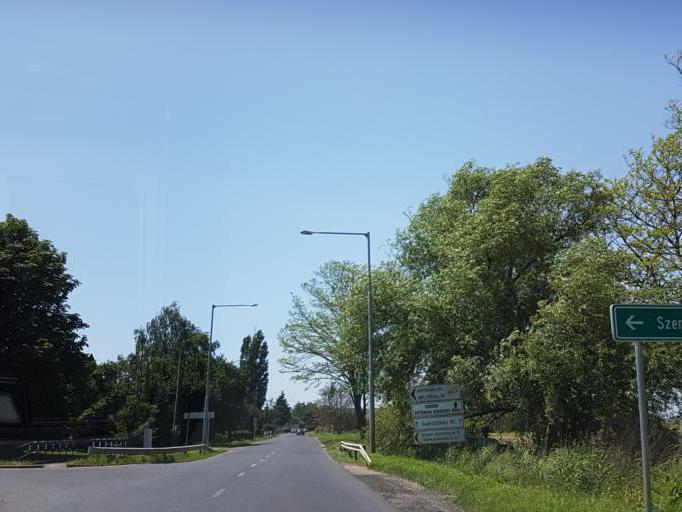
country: HU
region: Zala
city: Zalaegerszeg
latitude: 46.8565
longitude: 16.7997
